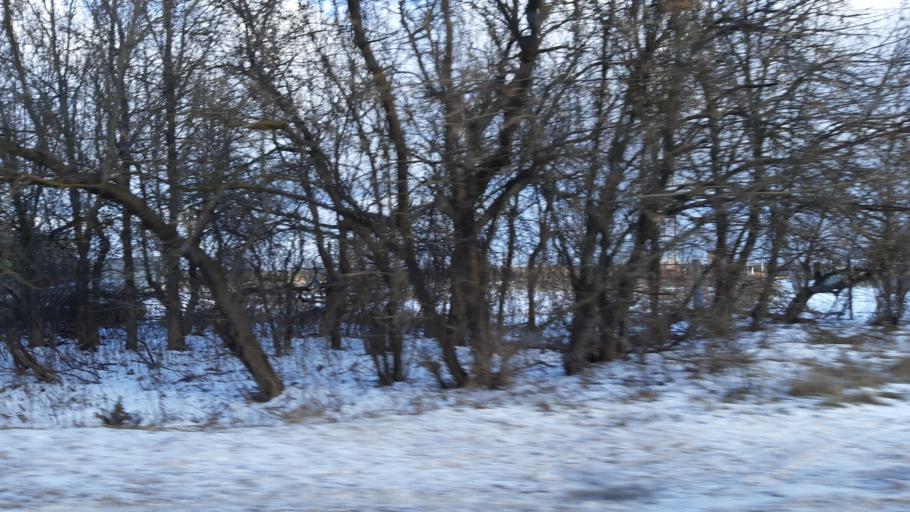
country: RU
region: Moskovskaya
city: Noginsk-9
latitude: 56.0487
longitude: 38.5515
